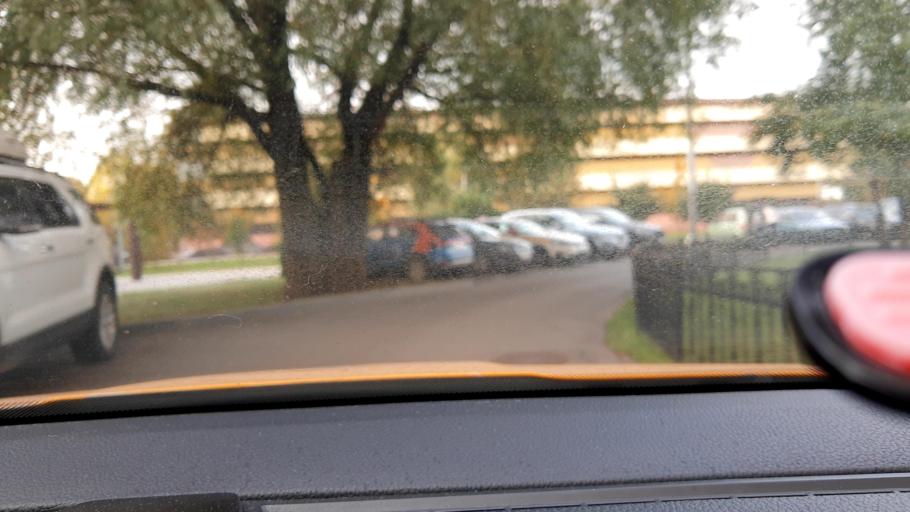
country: RU
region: Moskovskaya
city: Mosrentgen
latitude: 55.6284
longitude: 37.4761
